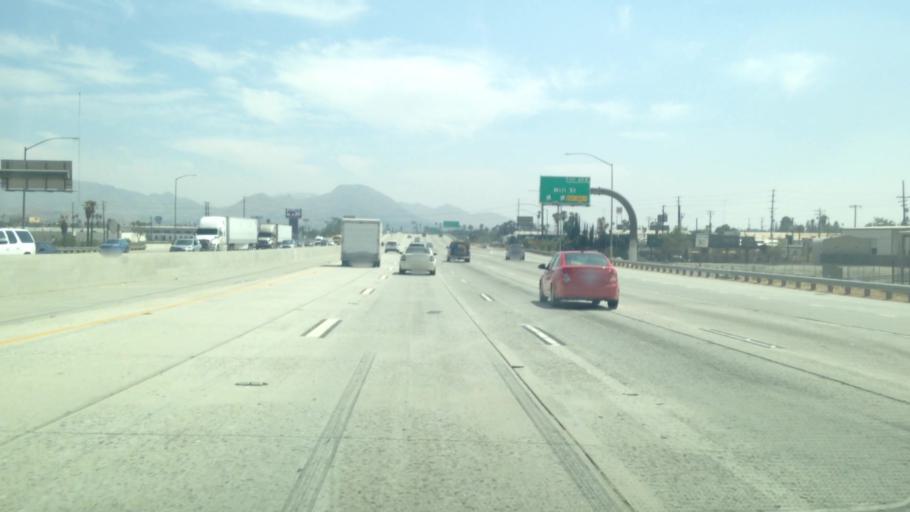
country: US
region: California
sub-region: San Bernardino County
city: San Bernardino
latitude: 34.0973
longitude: -117.3023
